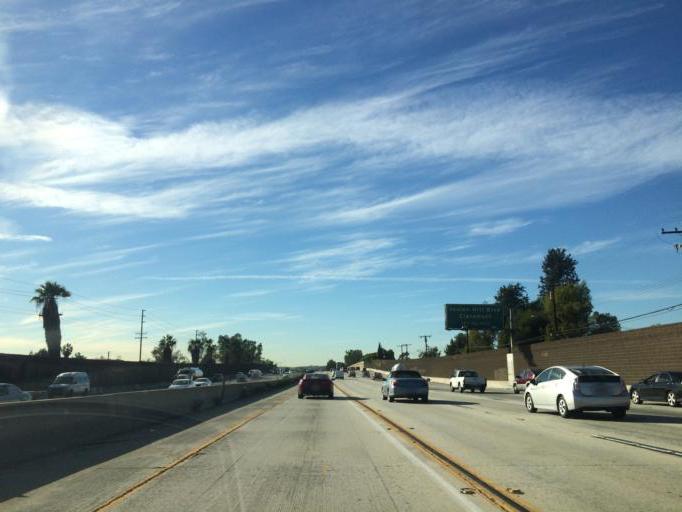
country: US
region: California
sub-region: San Bernardino County
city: Montclair
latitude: 34.0819
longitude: -117.7068
